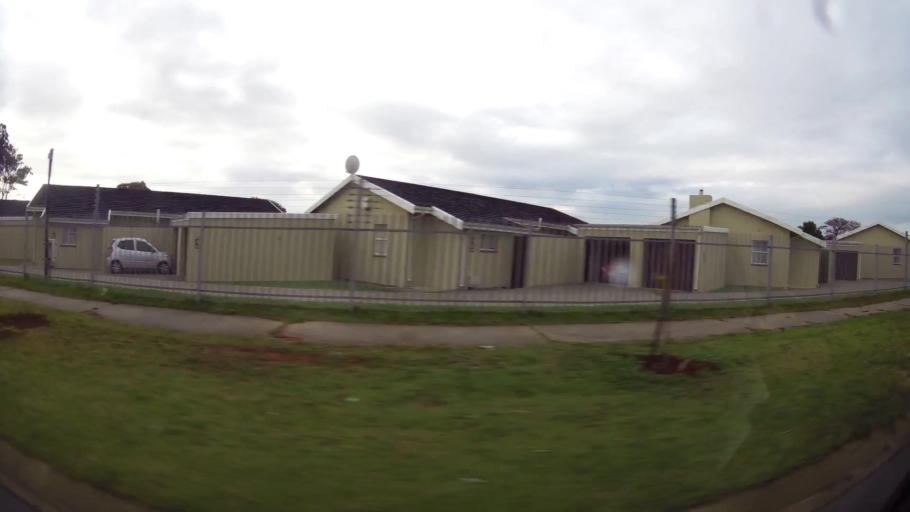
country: ZA
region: Eastern Cape
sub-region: Nelson Mandela Bay Metropolitan Municipality
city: Port Elizabeth
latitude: -33.9825
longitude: 25.5588
